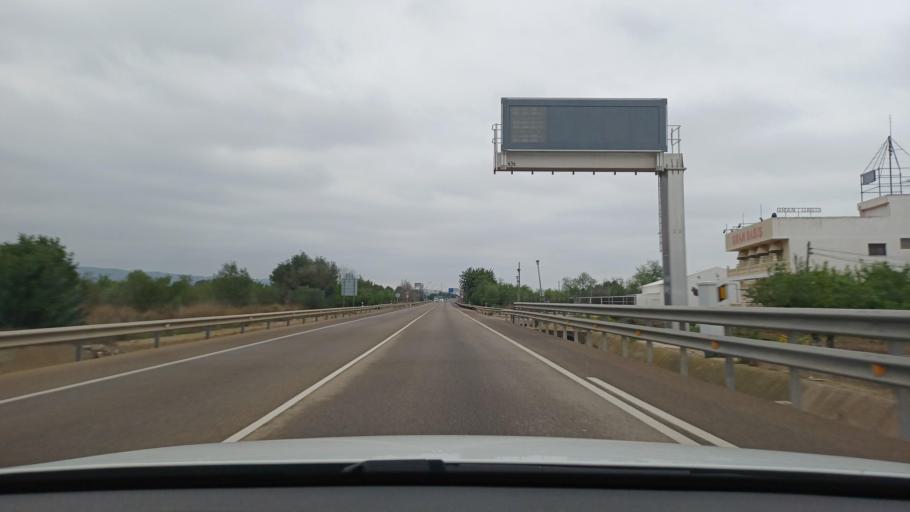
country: ES
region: Valencia
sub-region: Provincia de Castello
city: Orpesa/Oropesa del Mar
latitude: 40.0995
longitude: 0.1345
